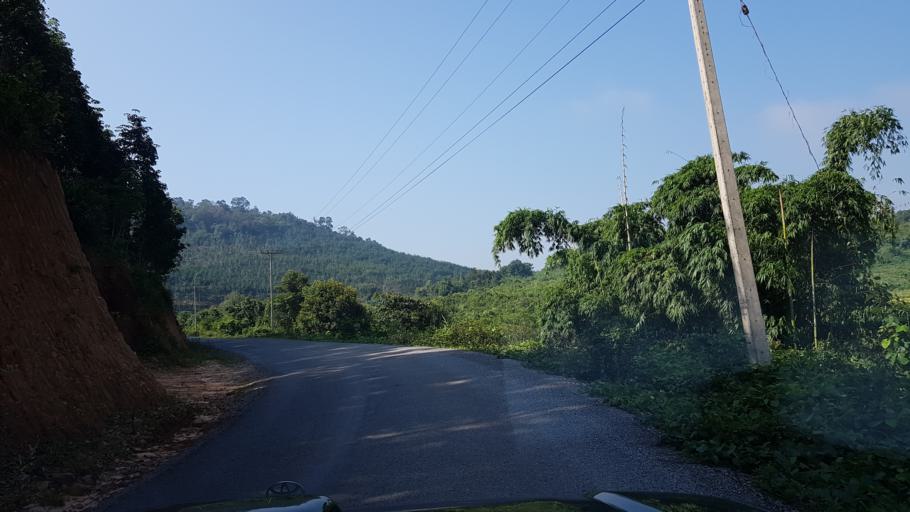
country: LA
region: Oudomxai
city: Muang Xay
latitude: 20.7150
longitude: 102.0746
